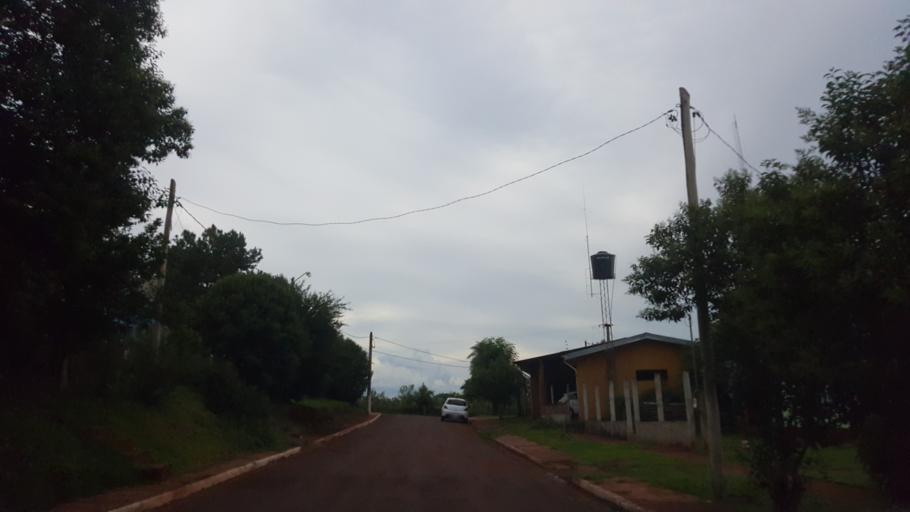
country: AR
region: Misiones
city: Santo Pipo
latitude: -27.1069
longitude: -55.3784
